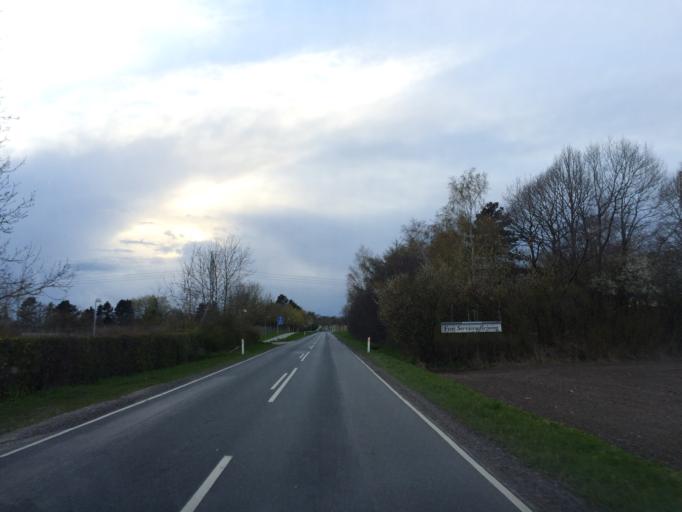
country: DK
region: South Denmark
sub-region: Odense Kommune
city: Bellinge
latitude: 55.3442
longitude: 10.2846
